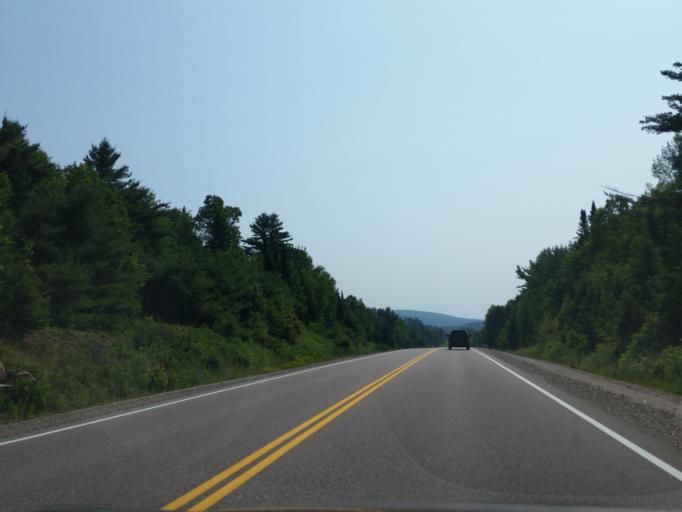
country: CA
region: Ontario
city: Mattawa
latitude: 46.3055
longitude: -78.6052
